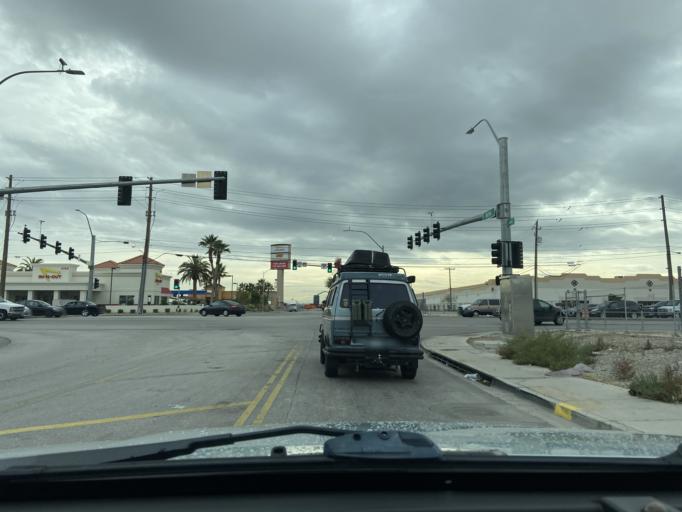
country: US
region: Nevada
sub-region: Clark County
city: North Las Vegas
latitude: 36.2404
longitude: -115.1120
